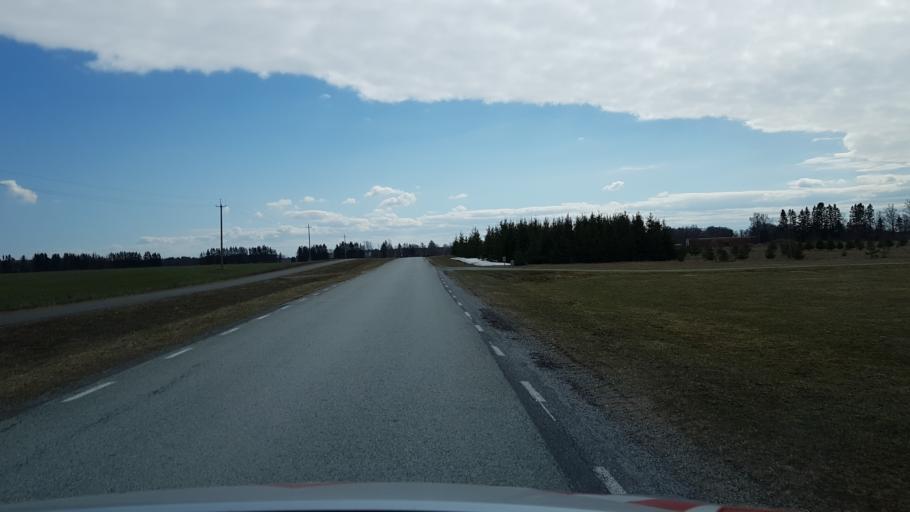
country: EE
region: Laeaene-Virumaa
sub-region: Haljala vald
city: Haljala
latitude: 59.4037
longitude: 26.2641
